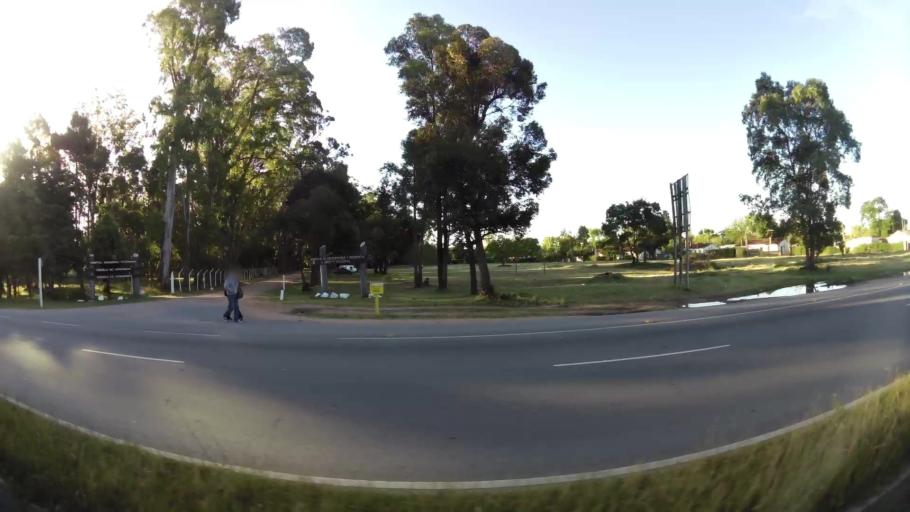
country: UY
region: Canelones
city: Paso de Carrasco
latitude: -34.8488
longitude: -56.0330
